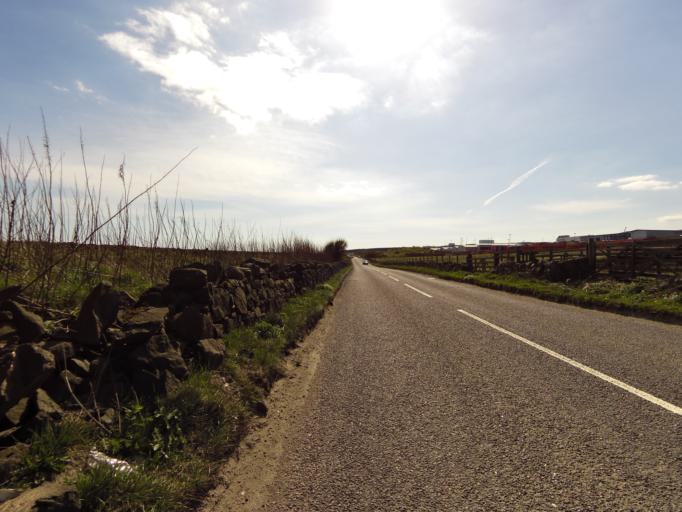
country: GB
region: Scotland
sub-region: Aberdeen City
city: Aberdeen
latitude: 57.1198
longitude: -2.0596
